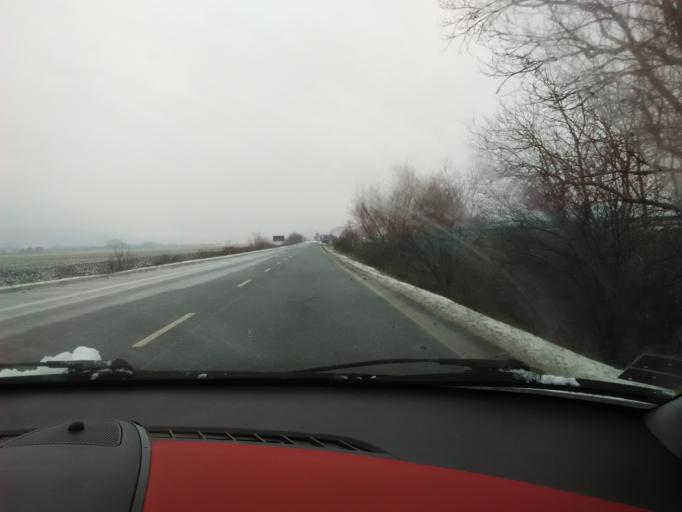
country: SK
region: Bratislavsky
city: Stupava
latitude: 48.2423
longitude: 16.9900
